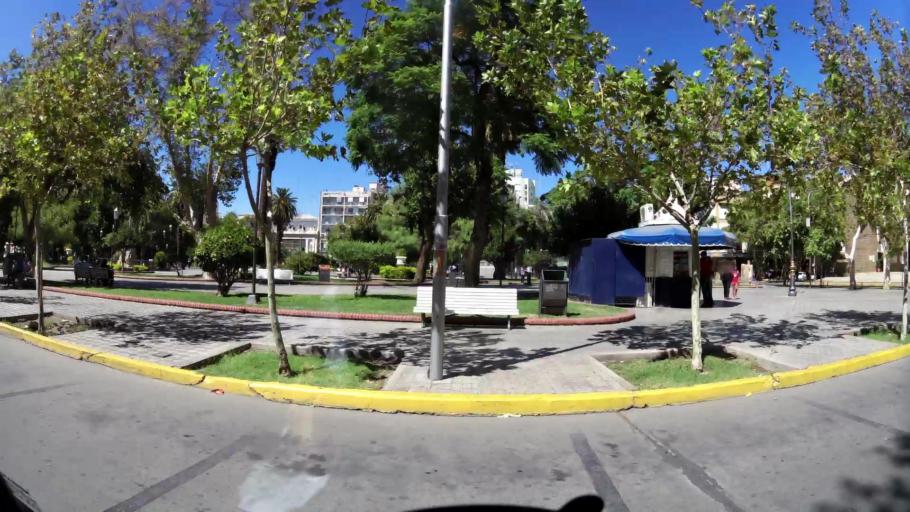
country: AR
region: San Juan
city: San Juan
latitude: -31.5367
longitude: -68.5254
